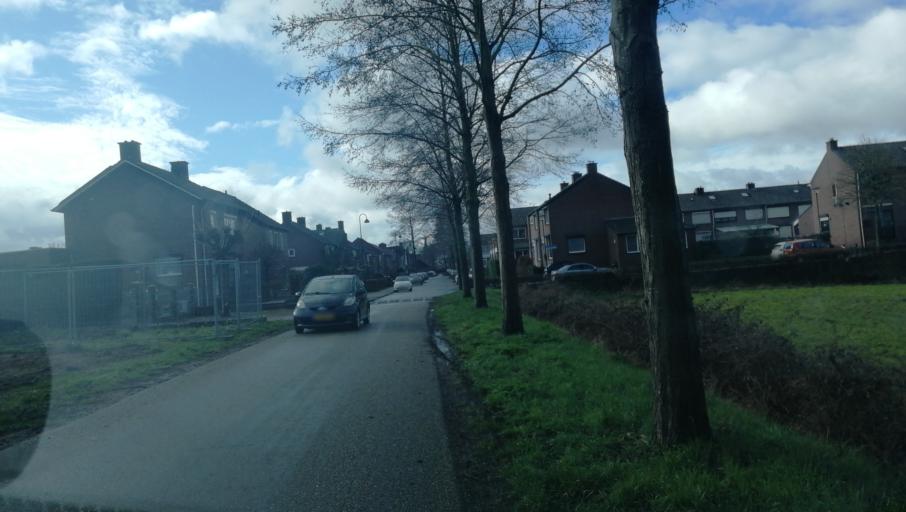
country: NL
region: Limburg
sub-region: Gemeente Venlo
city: Venlo
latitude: 51.4224
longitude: 6.1667
